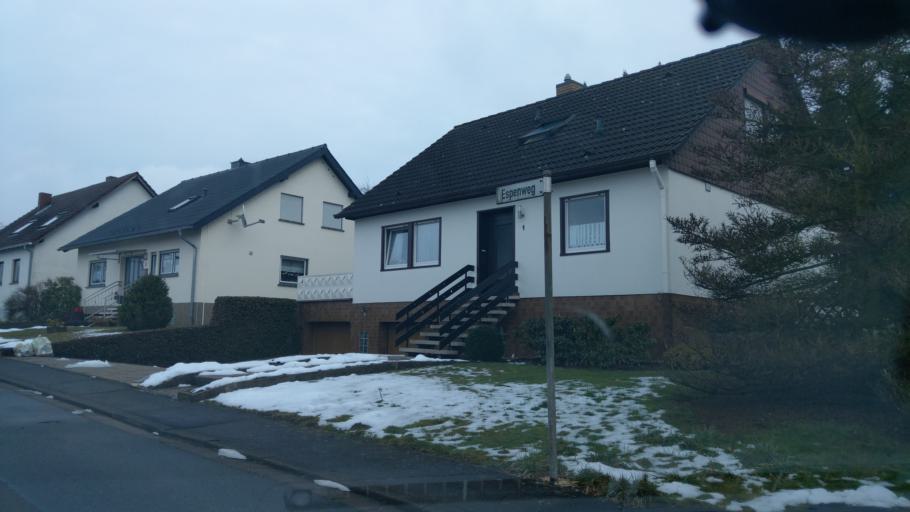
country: DE
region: Saarland
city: Hangard
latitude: 49.3675
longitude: 7.1988
